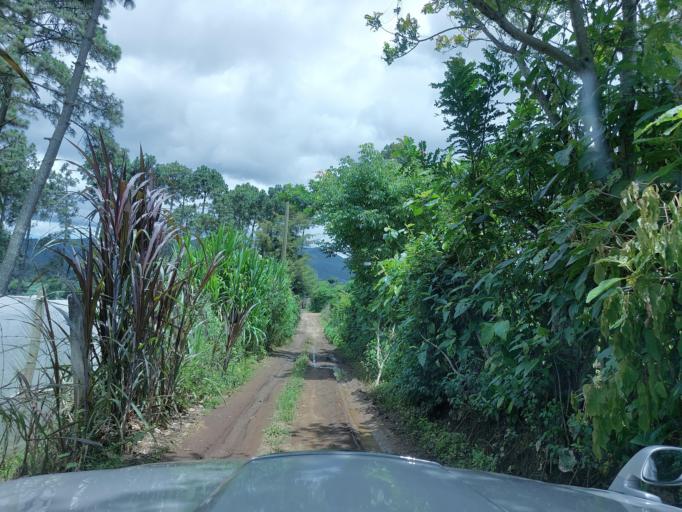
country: GT
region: Chimaltenango
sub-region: Municipio de Chimaltenango
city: Chimaltenango
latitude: 14.6419
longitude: -90.8294
